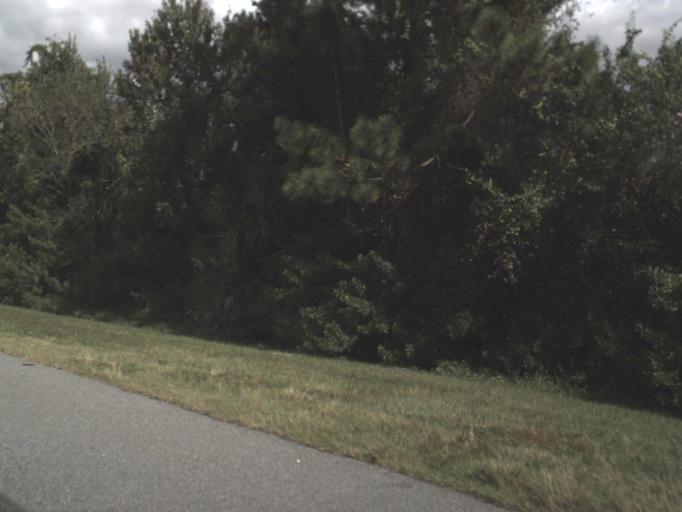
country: US
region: Florida
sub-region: Orange County
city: Southchase
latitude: 28.4167
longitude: -81.3918
